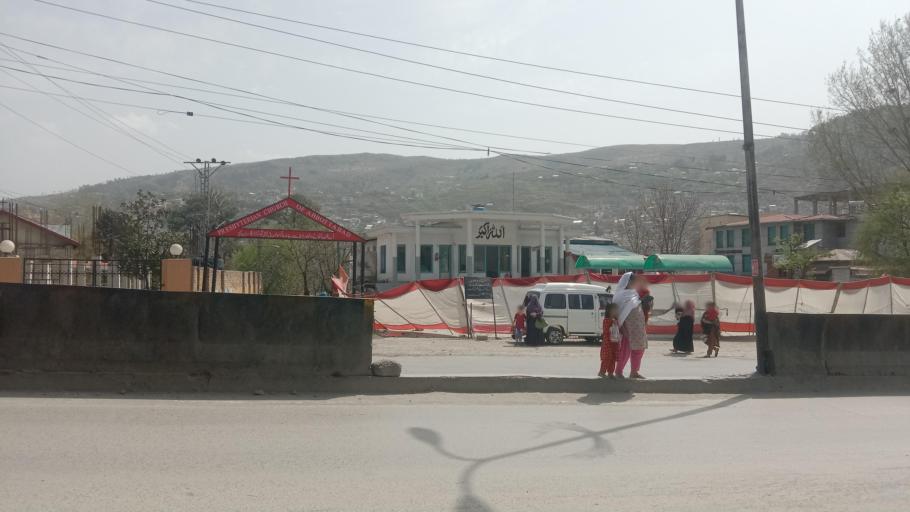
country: PK
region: Khyber Pakhtunkhwa
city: Abbottabad
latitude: 34.1486
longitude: 73.2160
